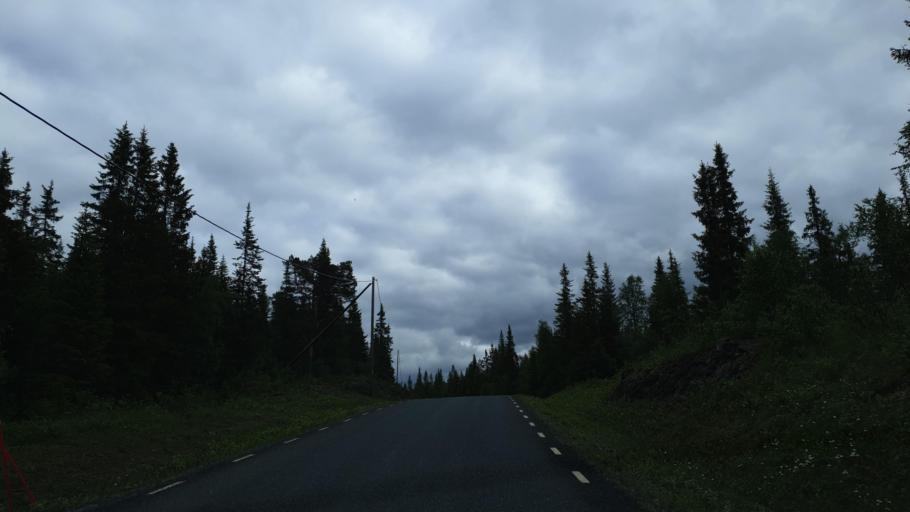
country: NO
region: Nordland
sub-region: Hattfjelldal
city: Hattfjelldal
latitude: 65.4315
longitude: 14.5889
